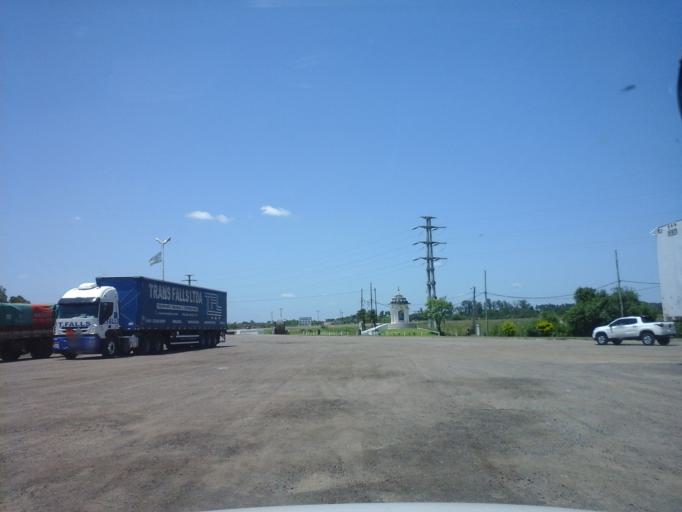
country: AR
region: Corrientes
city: Corrientes
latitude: -27.4370
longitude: -58.7348
